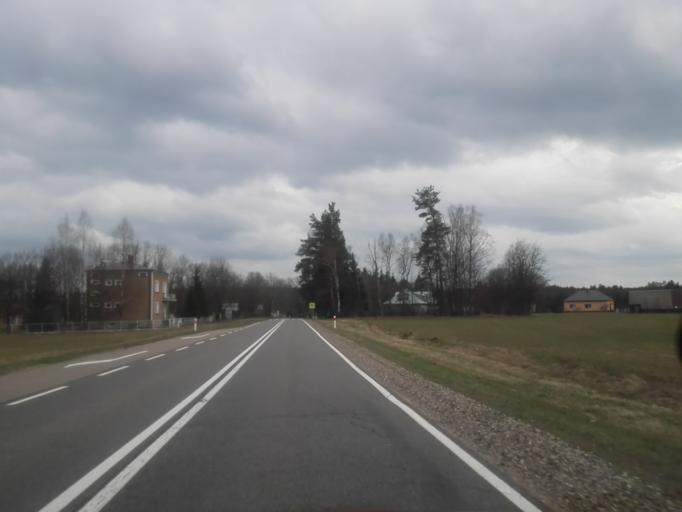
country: PL
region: Podlasie
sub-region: Powiat sejnenski
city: Sejny
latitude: 53.9820
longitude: 23.2942
